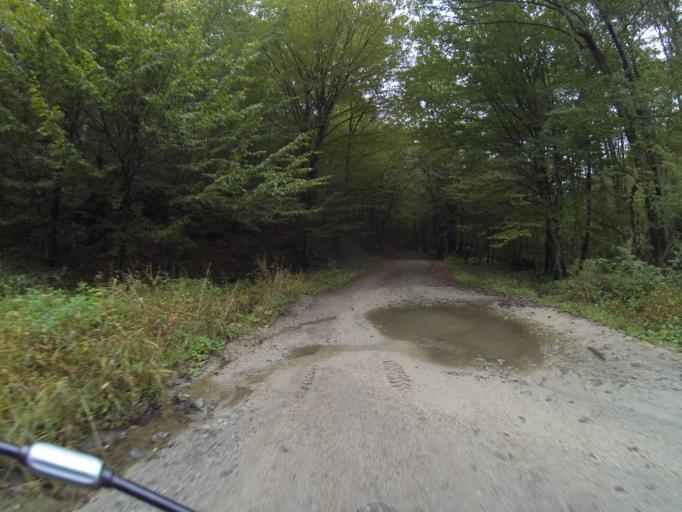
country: RO
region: Gorj
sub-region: Comuna Tismana
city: Sohodol
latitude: 45.0579
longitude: 22.9009
